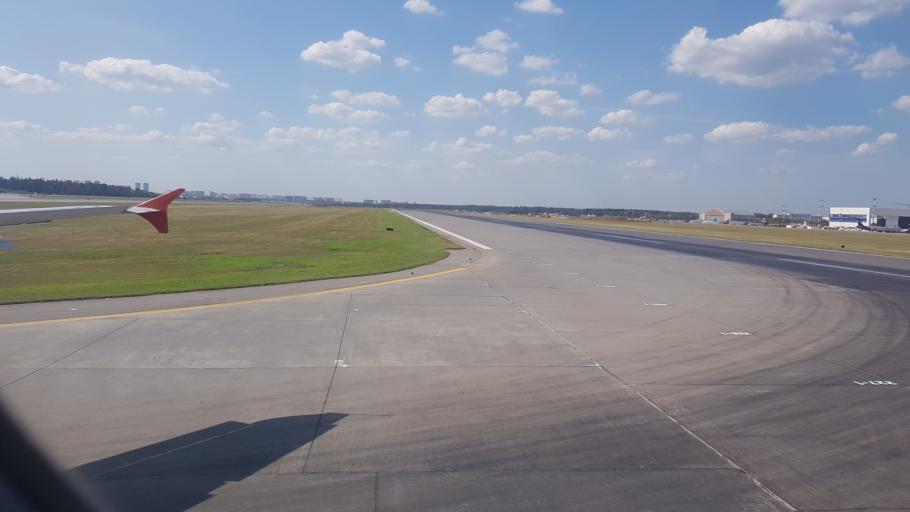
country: RU
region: Moskovskaya
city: Novopodrezkovo
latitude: 55.9733
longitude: 37.4128
